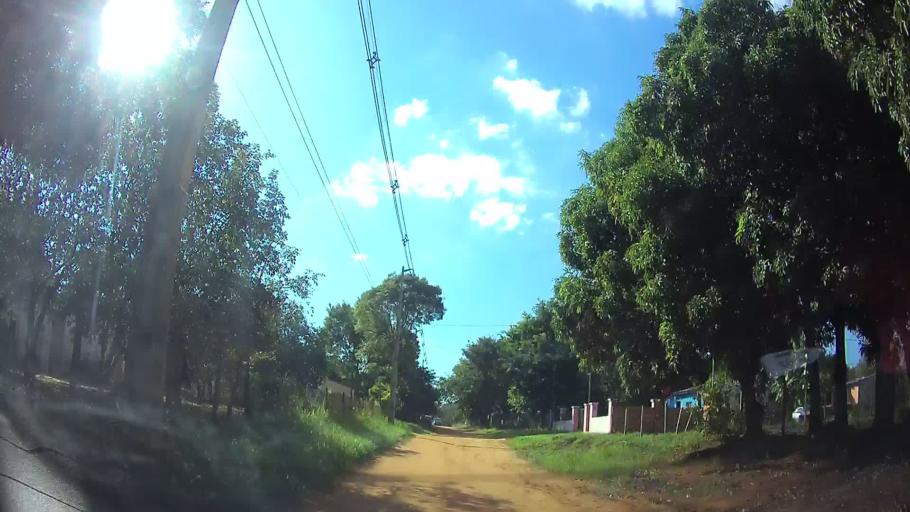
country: PY
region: Central
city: Limpio
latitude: -25.2495
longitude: -57.4748
